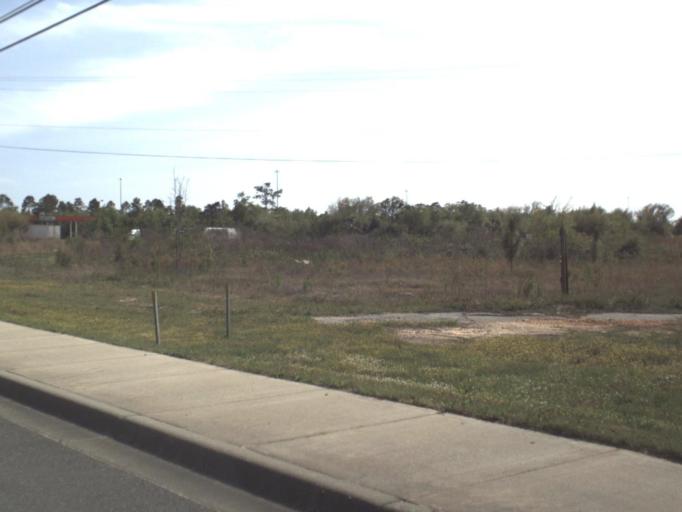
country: US
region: Florida
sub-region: Santa Rosa County
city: East Milton
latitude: 30.6227
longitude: -86.9654
